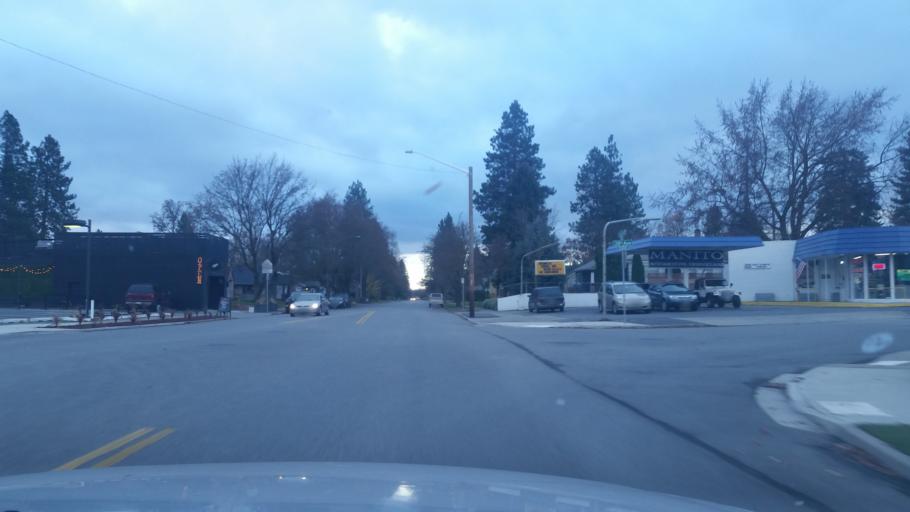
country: US
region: Washington
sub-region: Spokane County
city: Spokane
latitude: 47.6202
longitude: -117.4021
